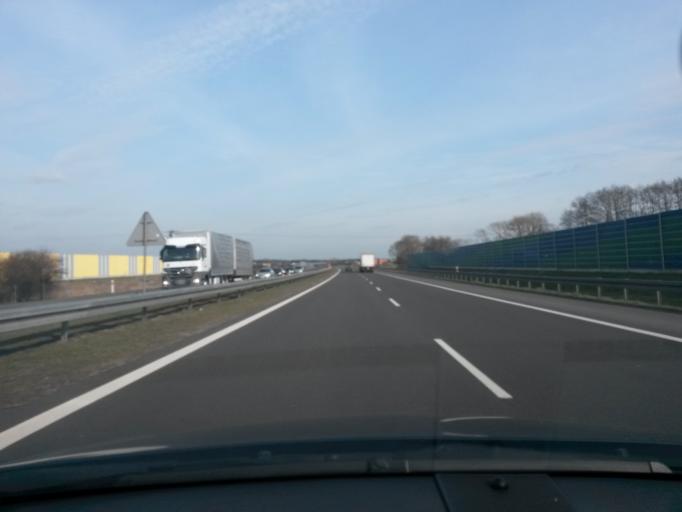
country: PL
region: Greater Poland Voivodeship
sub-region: Powiat wrzesinski
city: Wrzesnia
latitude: 52.3109
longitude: 17.5575
